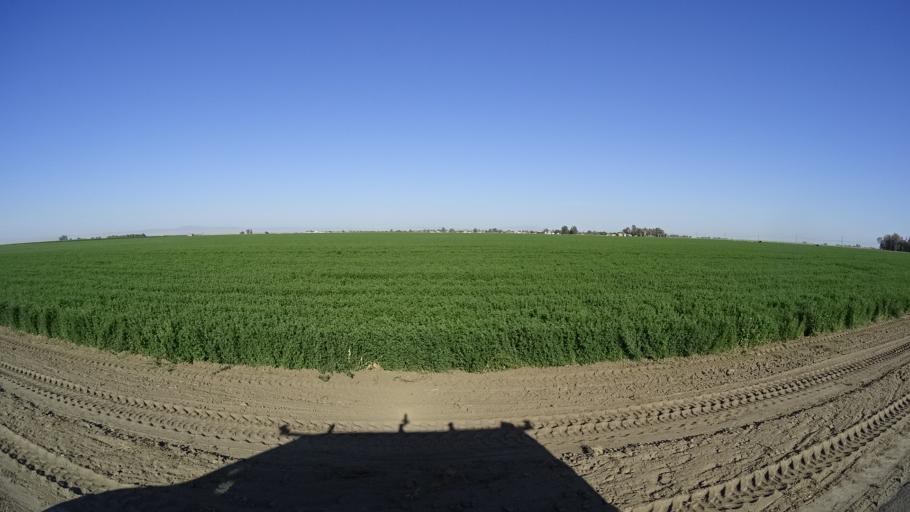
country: US
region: California
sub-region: Kings County
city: Stratford
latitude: 36.1861
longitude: -119.7984
